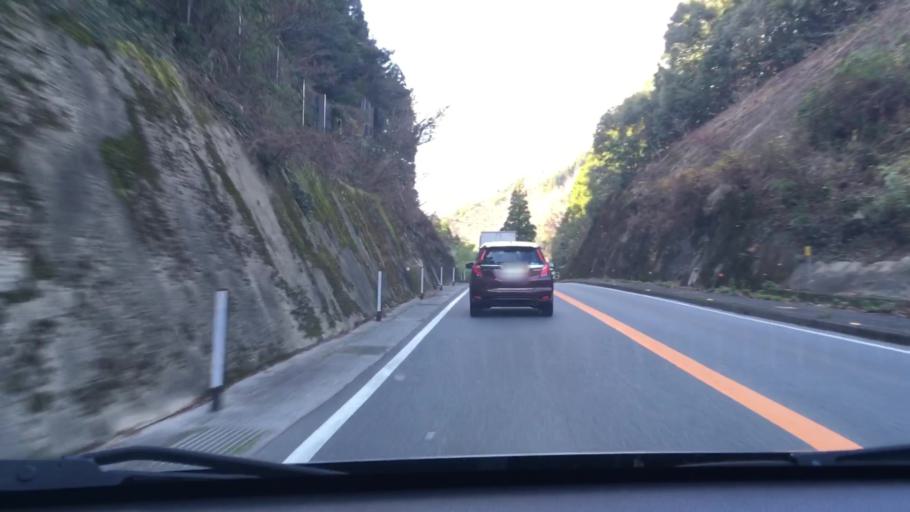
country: JP
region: Oita
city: Tsukumiura
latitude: 33.0002
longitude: 131.8128
